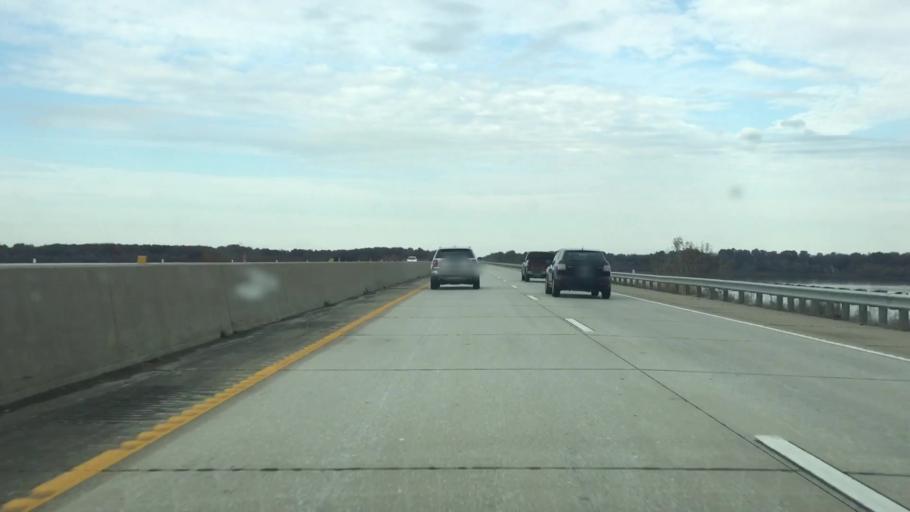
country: US
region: Missouri
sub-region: Henry County
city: Clinton
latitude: 38.2780
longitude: -93.7596
